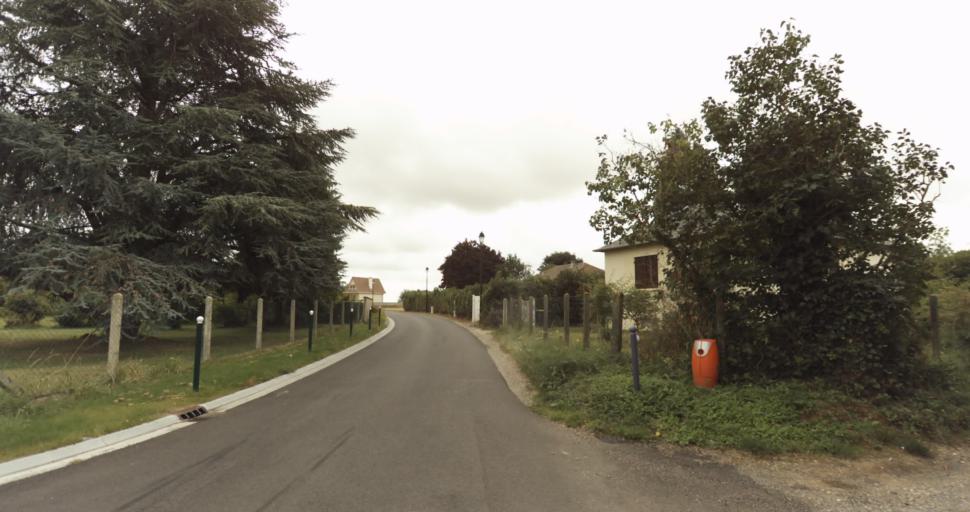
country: FR
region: Haute-Normandie
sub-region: Departement de l'Eure
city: La Couture-Boussey
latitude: 48.9439
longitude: 1.3681
